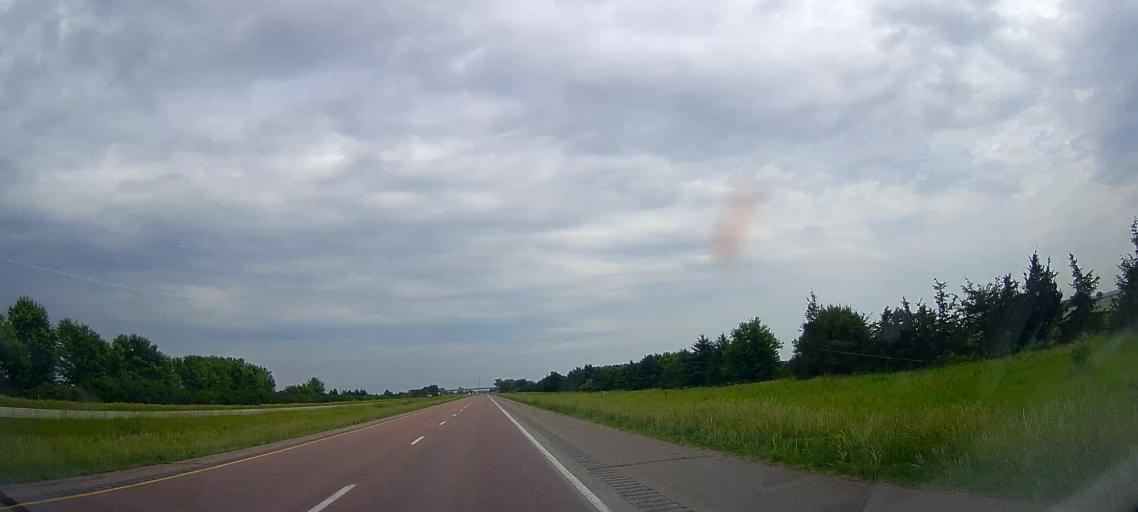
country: US
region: Iowa
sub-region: Woodbury County
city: Sergeant Bluff
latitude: 42.2625
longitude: -96.2621
